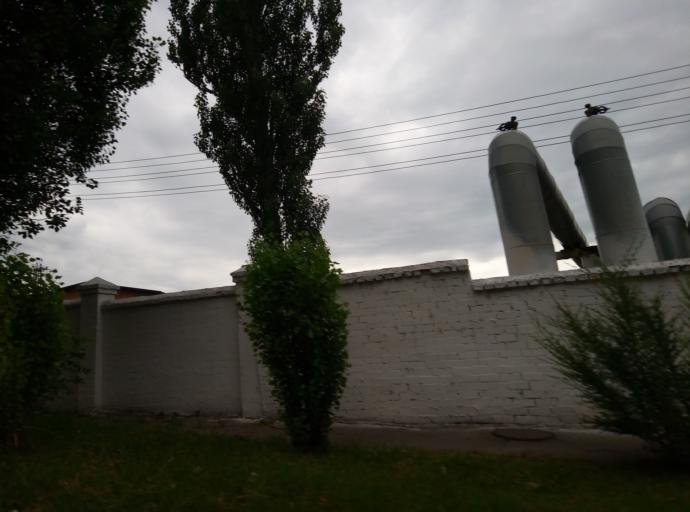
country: RU
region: Kursk
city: Kursk
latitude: 51.7079
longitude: 36.1635
